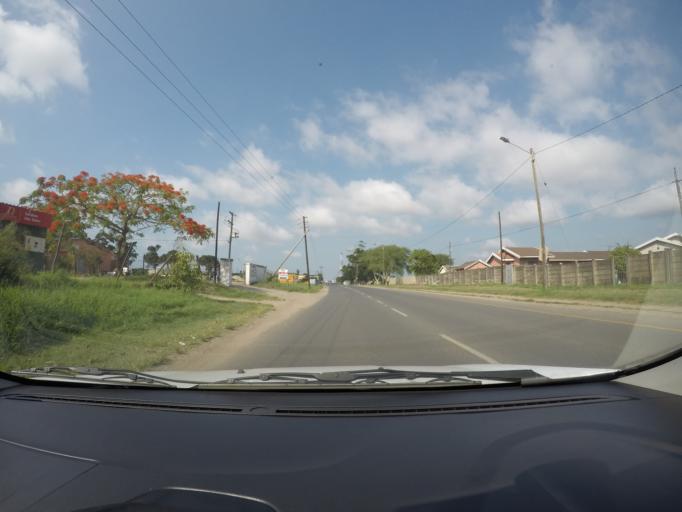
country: ZA
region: KwaZulu-Natal
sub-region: uThungulu District Municipality
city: eSikhawini
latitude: -28.8729
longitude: 31.9193
